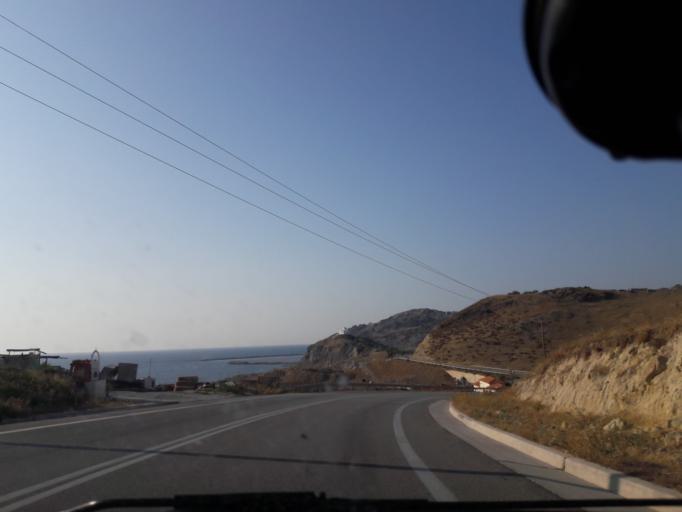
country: GR
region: North Aegean
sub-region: Nomos Lesvou
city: Myrina
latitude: 39.8628
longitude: 25.0557
